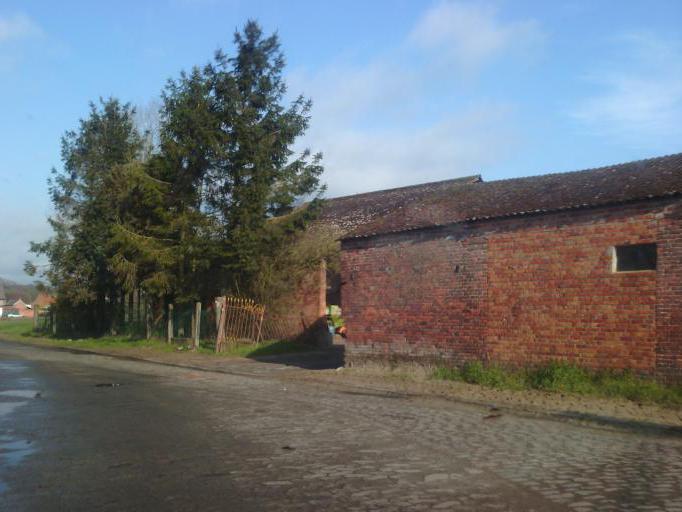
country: BE
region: Flanders
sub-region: Provincie Oost-Vlaanderen
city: Berlare
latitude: 51.0492
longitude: 4.0165
